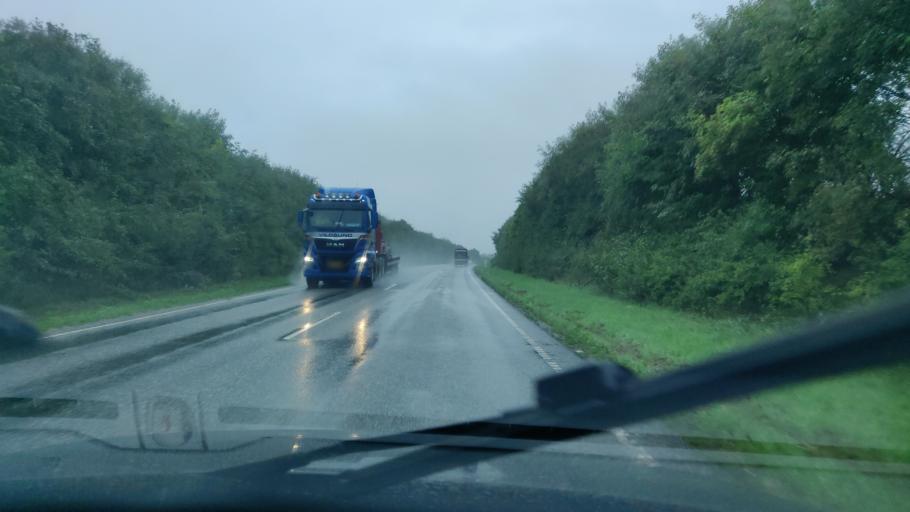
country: DK
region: North Denmark
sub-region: Thisted Kommune
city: Thisted
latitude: 56.9744
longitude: 8.6868
